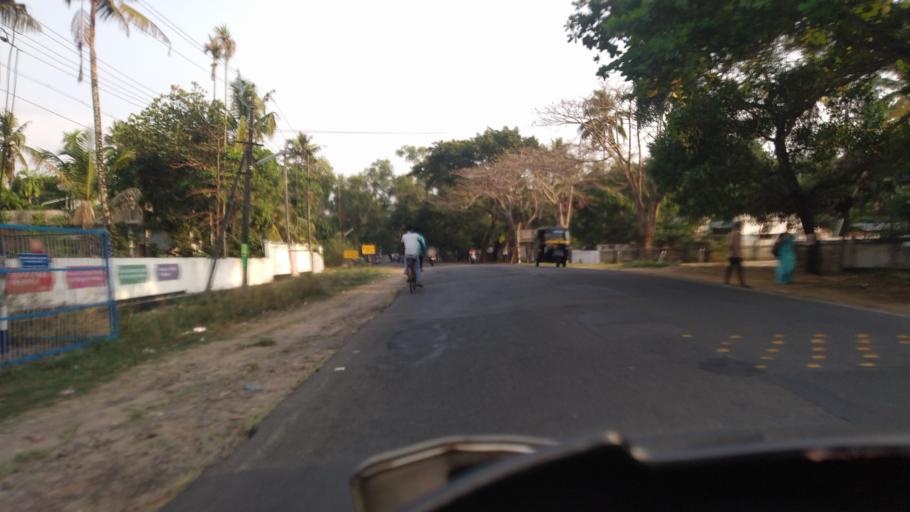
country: IN
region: Kerala
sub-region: Thrissur District
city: Thanniyam
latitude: 10.3661
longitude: 76.1234
